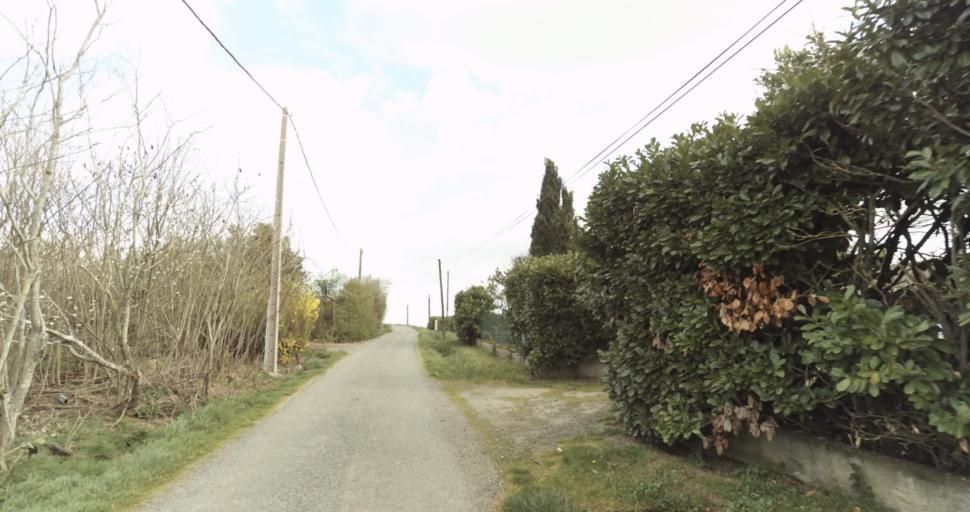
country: FR
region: Midi-Pyrenees
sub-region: Departement de la Haute-Garonne
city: Auterive
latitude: 43.3665
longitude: 1.4856
